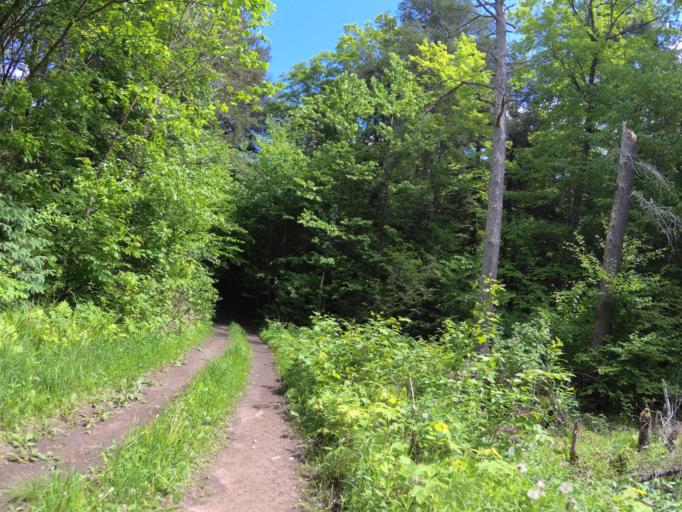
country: CA
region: Ontario
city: Renfrew
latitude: 45.0578
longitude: -76.8527
